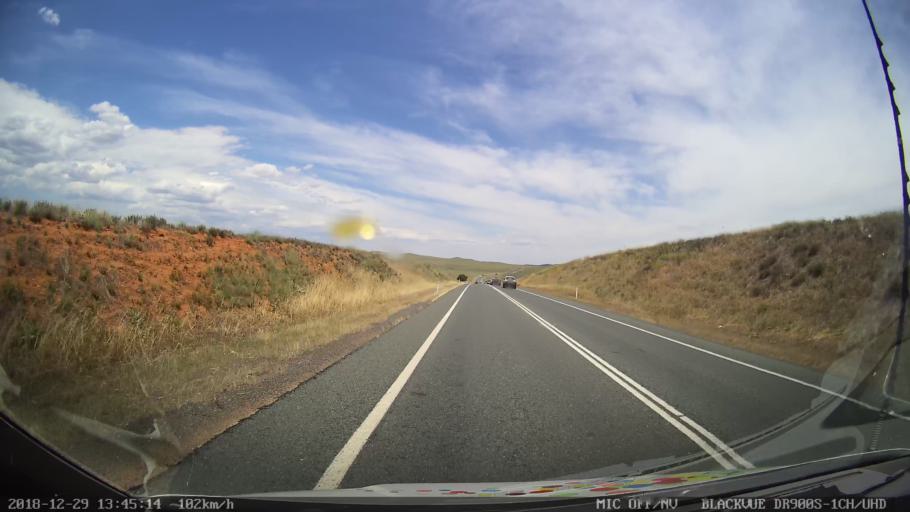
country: AU
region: New South Wales
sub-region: Cooma-Monaro
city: Cooma
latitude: -36.0934
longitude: 149.1452
